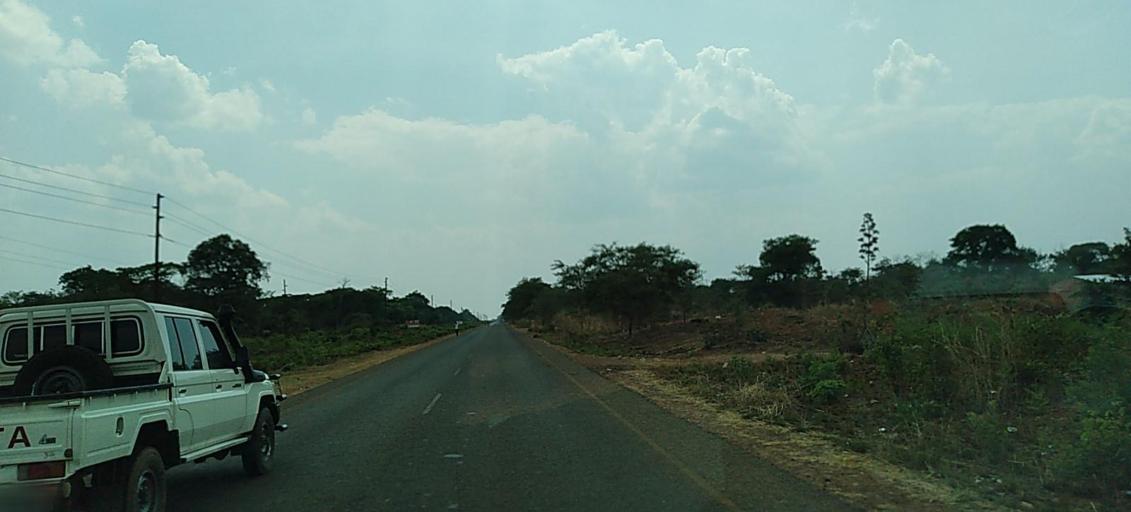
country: ZM
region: Copperbelt
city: Chingola
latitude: -12.8567
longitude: 27.6400
